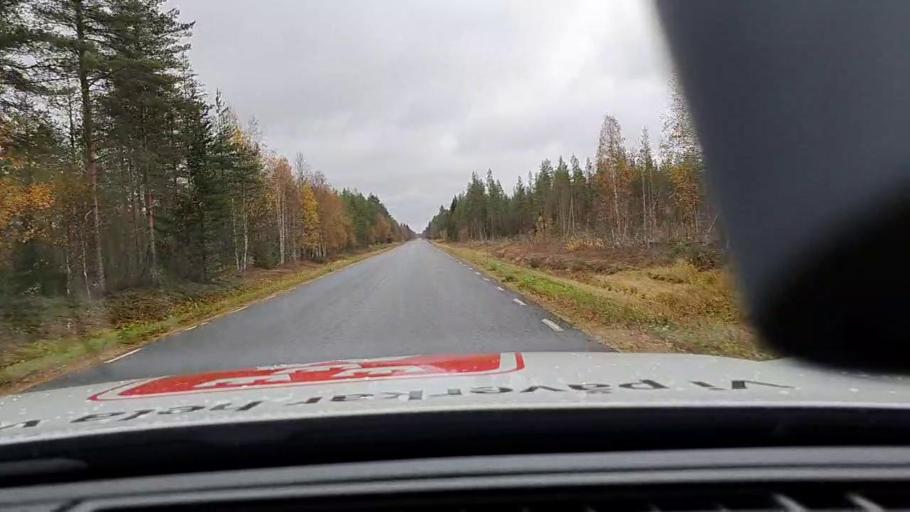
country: SE
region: Norrbotten
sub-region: Haparanda Kommun
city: Haparanda
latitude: 65.9086
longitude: 23.8308
